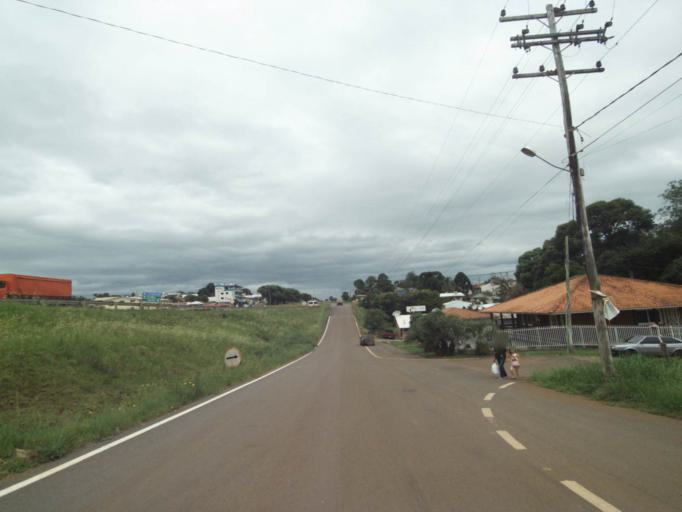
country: BR
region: Rio Grande do Sul
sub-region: Lagoa Vermelha
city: Lagoa Vermelha
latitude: -28.2043
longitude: -51.5235
